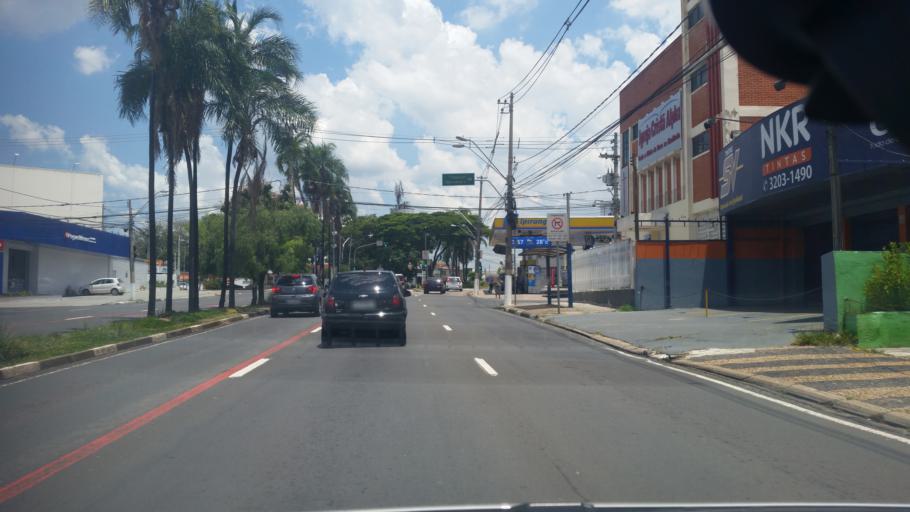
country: BR
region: Sao Paulo
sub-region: Campinas
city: Campinas
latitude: -22.8767
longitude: -47.0449
